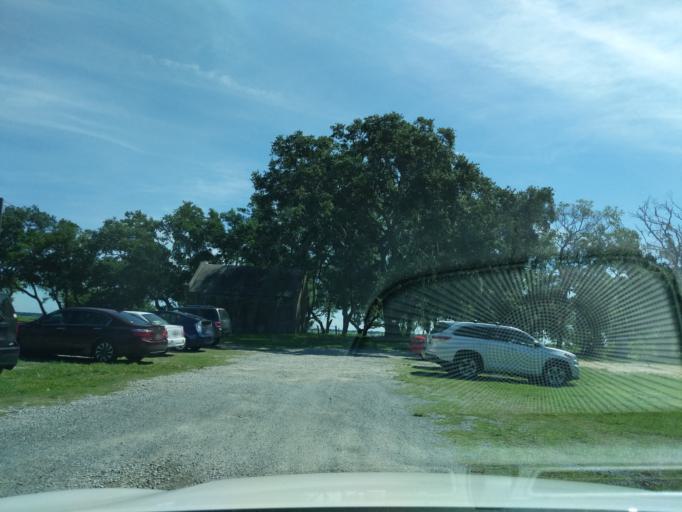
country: US
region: South Carolina
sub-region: Charleston County
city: Charleston
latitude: 32.7513
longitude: -79.8983
